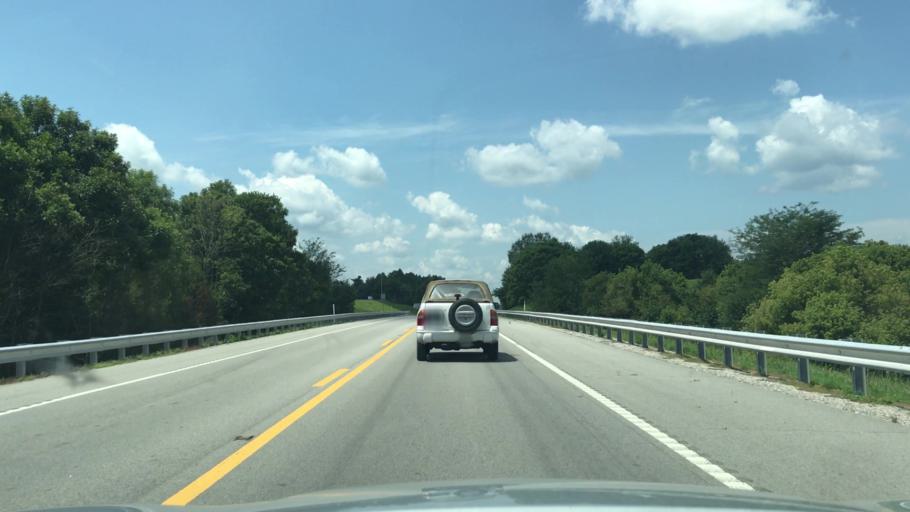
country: US
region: Tennessee
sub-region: Pickett County
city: Byrdstown
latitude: 36.6106
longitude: -85.1048
